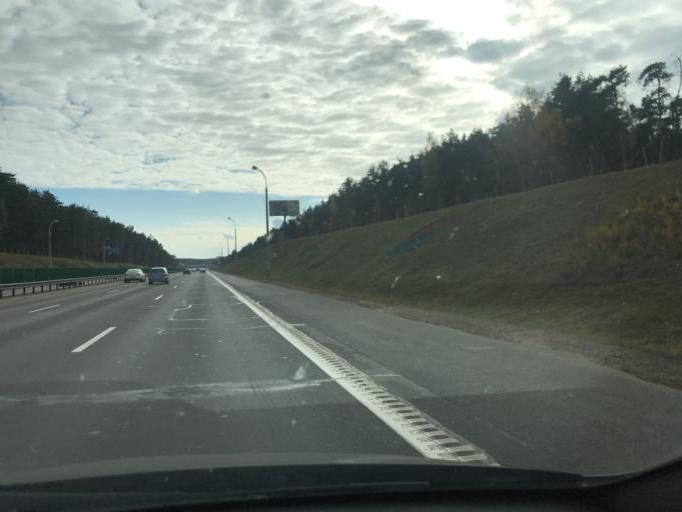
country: BY
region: Minsk
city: Vyaliki Trastsyanets
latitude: 53.8992
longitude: 27.6900
